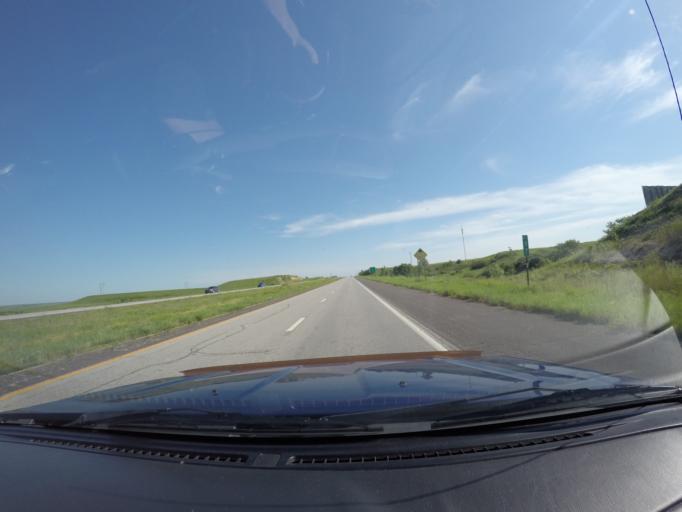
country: US
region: Kansas
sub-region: Riley County
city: Manhattan
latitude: 39.0722
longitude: -96.5385
